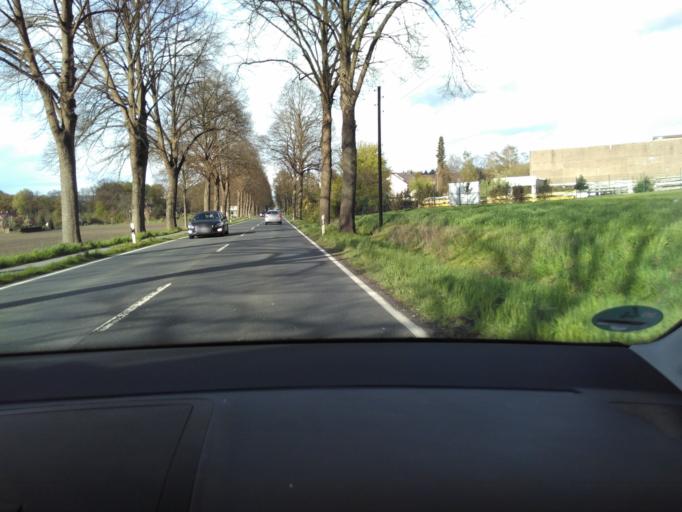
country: DE
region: North Rhine-Westphalia
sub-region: Regierungsbezirk Detmold
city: Steinhagen
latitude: 51.9605
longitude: 8.4505
